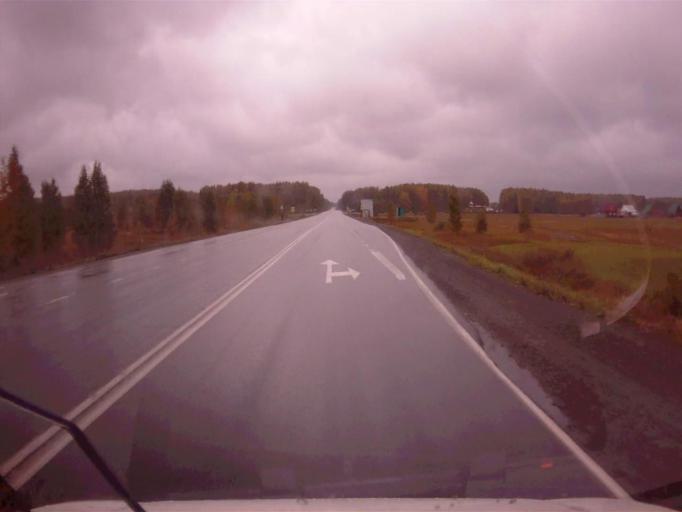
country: RU
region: Chelyabinsk
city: Argayash
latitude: 55.4557
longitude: 60.9284
